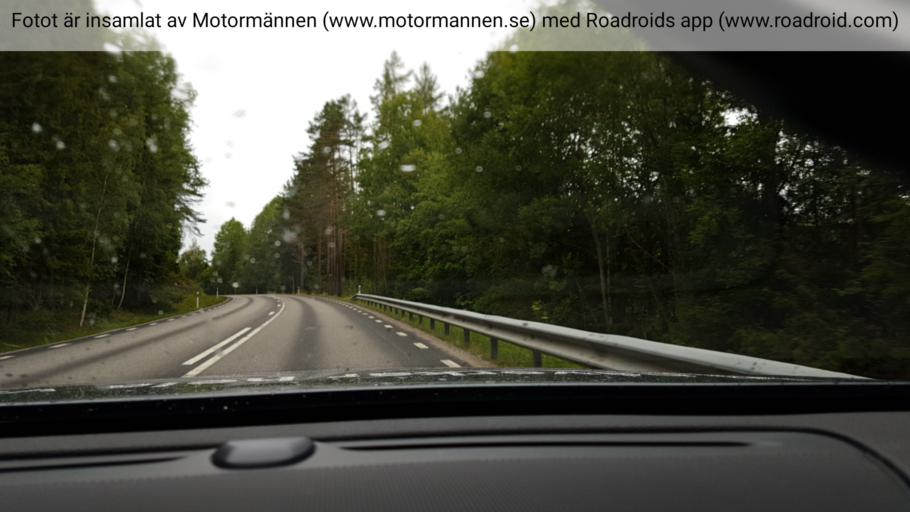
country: SE
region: Dalarna
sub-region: Faluns Kommun
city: Bjursas
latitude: 60.7389
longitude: 15.4294
